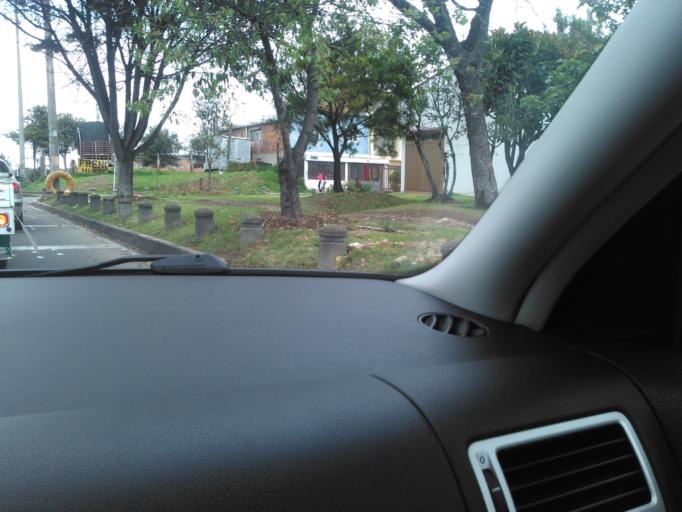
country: CO
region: Bogota D.C.
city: Bogota
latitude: 4.6125
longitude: -74.1213
